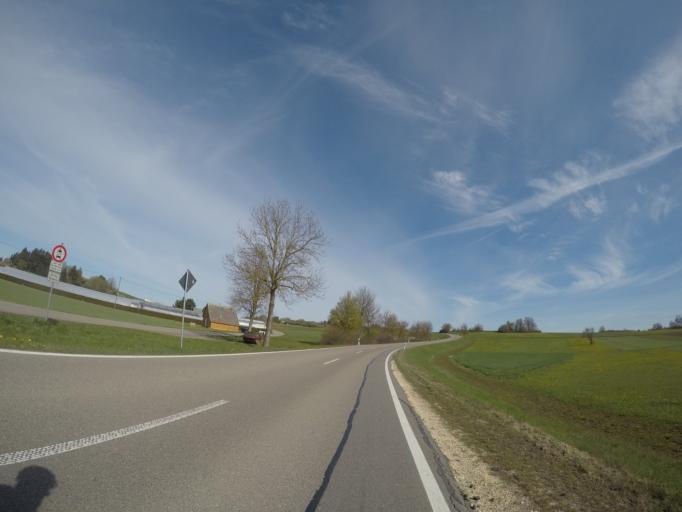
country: DE
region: Baden-Wuerttemberg
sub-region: Tuebingen Region
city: Laichingen
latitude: 48.4965
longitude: 9.6783
